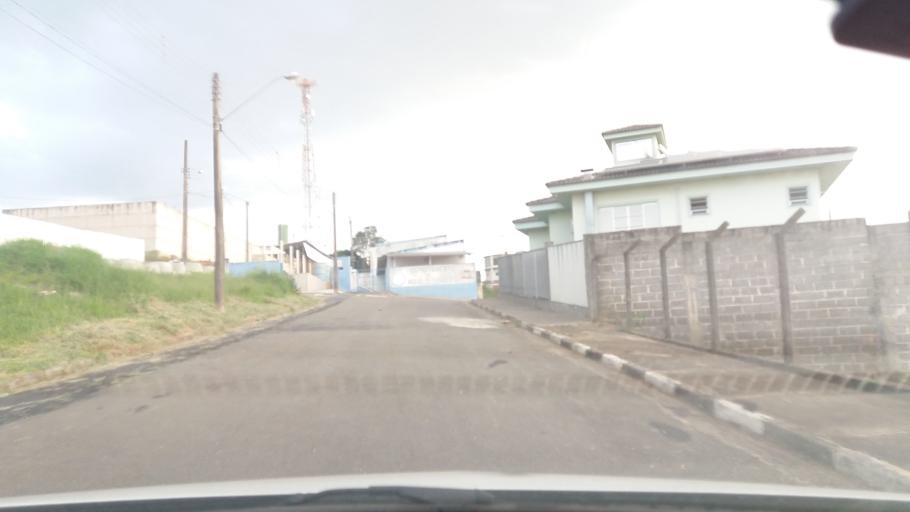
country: BR
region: Sao Paulo
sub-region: Bom Jesus Dos Perdoes
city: Bom Jesus dos Perdoes
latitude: -23.1436
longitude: -46.4653
